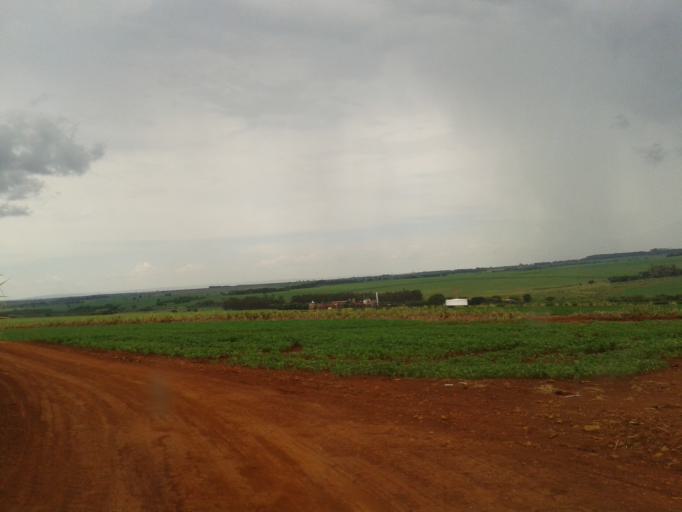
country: BR
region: Minas Gerais
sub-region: Centralina
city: Centralina
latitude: -18.6563
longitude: -49.2476
